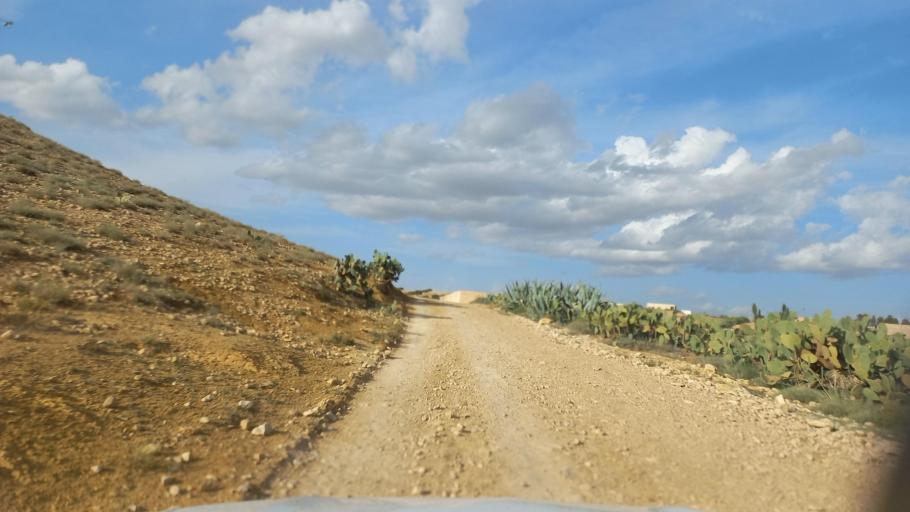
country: TN
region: Al Qasrayn
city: Sbiba
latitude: 35.4521
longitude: 9.0832
